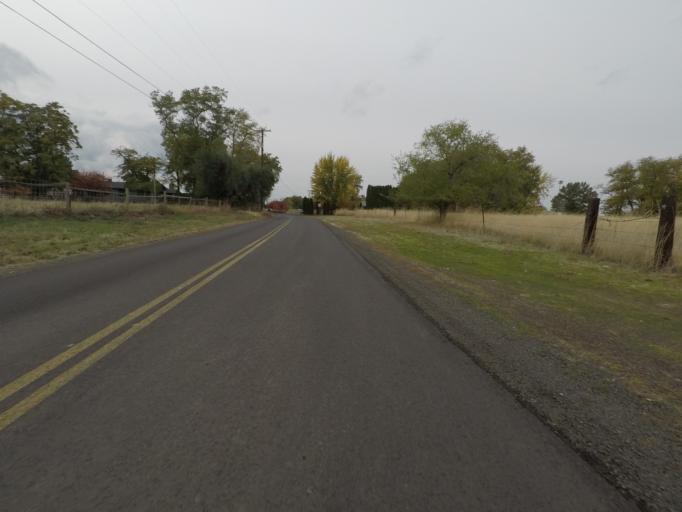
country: US
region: Washington
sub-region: Walla Walla County
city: Walla Walla East
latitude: 46.0750
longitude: -118.2773
